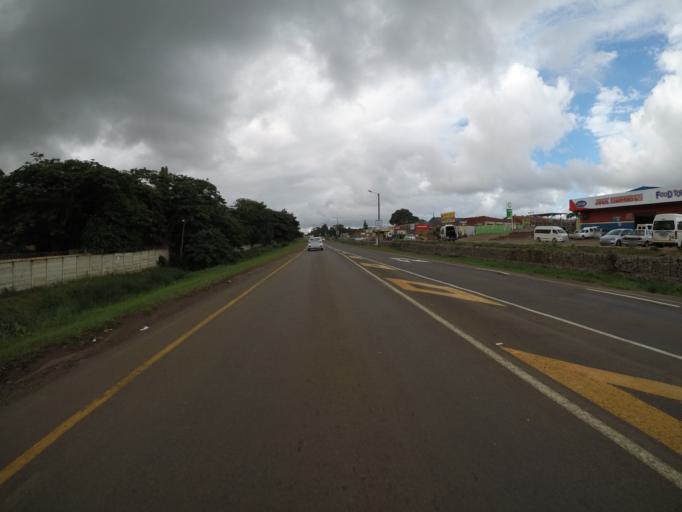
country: ZA
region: KwaZulu-Natal
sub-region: uMkhanyakude District Municipality
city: Mtubatuba
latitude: -28.4135
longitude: 32.1841
